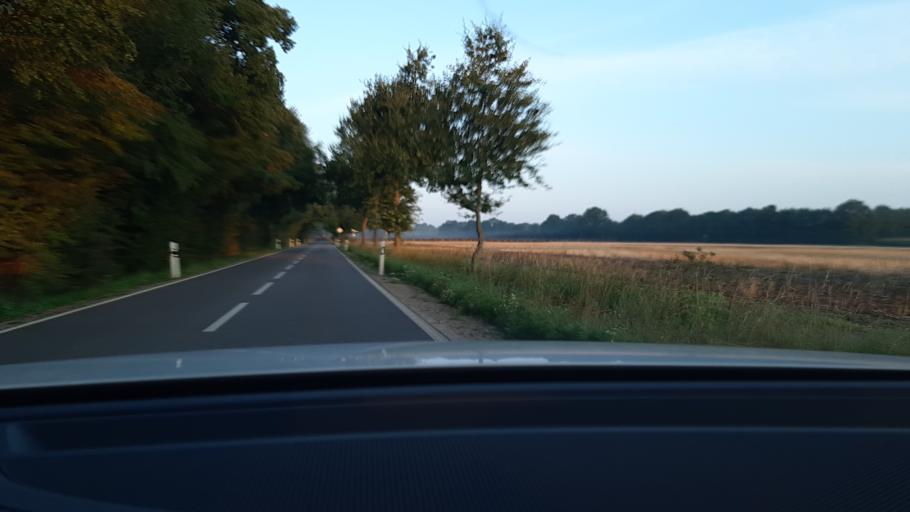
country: DE
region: Schleswig-Holstein
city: Hamberge
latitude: 53.8210
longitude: 10.5839
